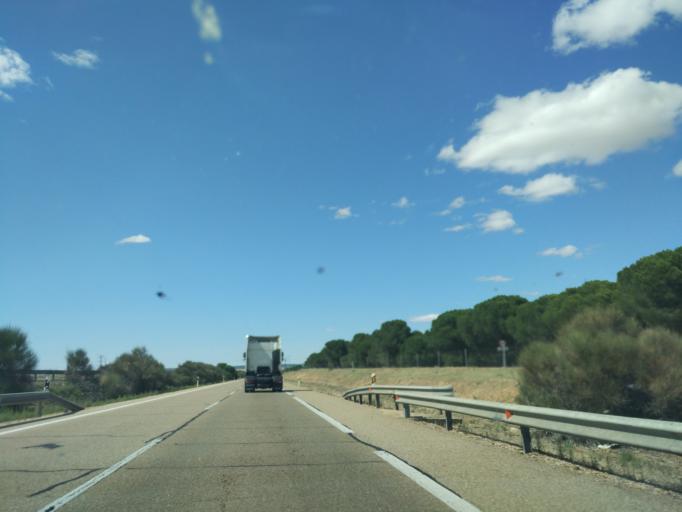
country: ES
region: Castille and Leon
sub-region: Provincia de Valladolid
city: Tordesillas
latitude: 41.4582
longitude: -4.9829
